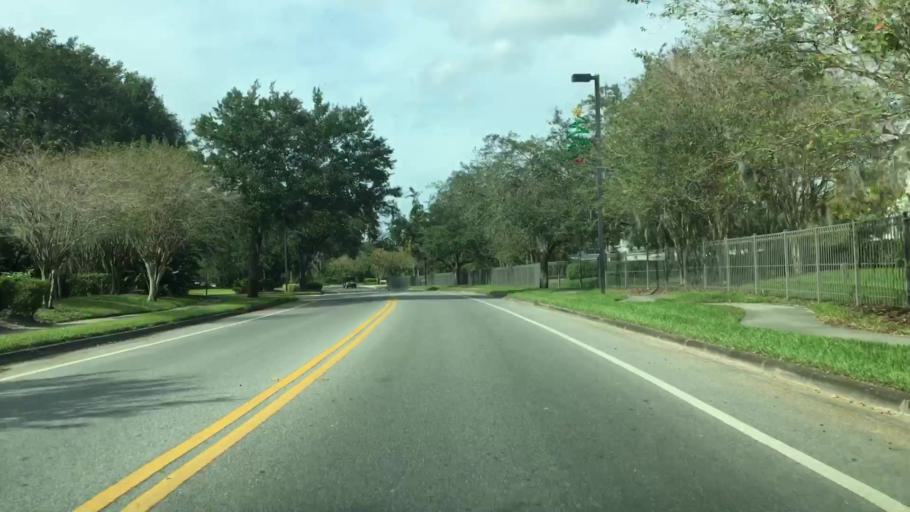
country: US
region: Florida
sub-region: Orange County
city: Conway
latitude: 28.4733
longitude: -81.3050
